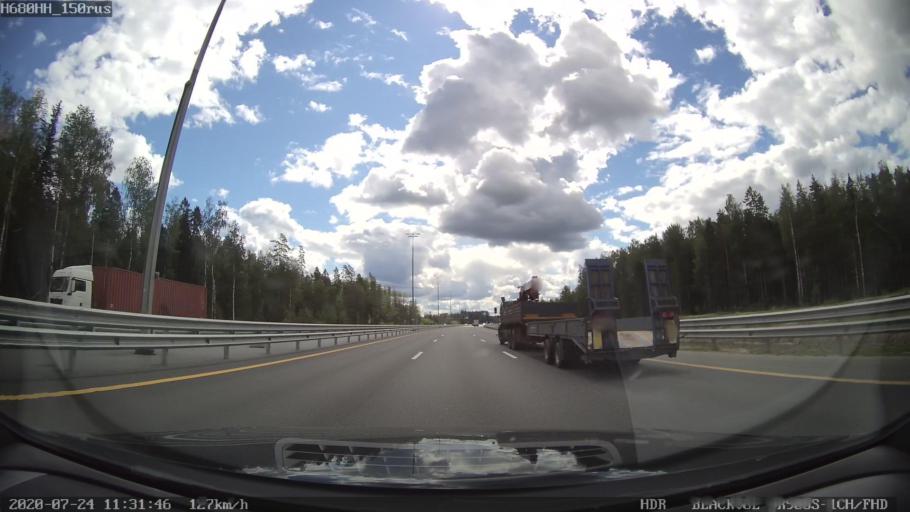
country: RU
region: Leningrad
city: Krasnyy Bor
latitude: 59.6520
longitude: 30.6448
